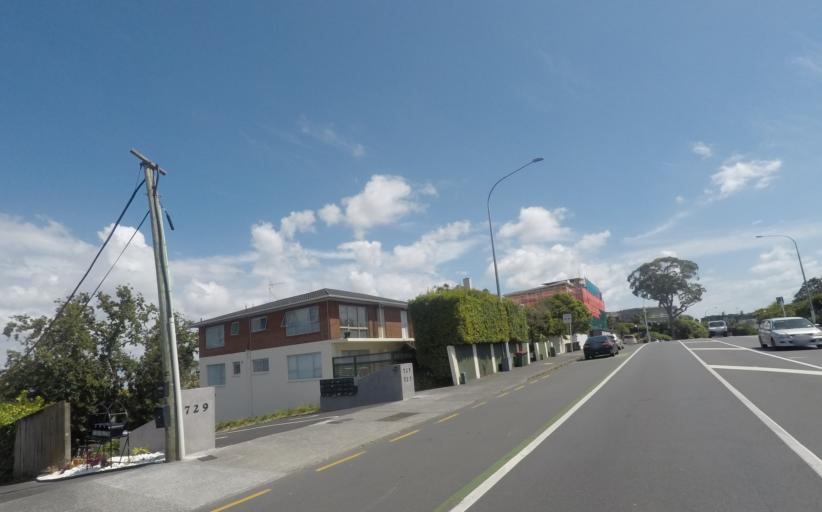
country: NZ
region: Auckland
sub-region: Auckland
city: Tamaki
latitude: -36.8789
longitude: 174.8227
